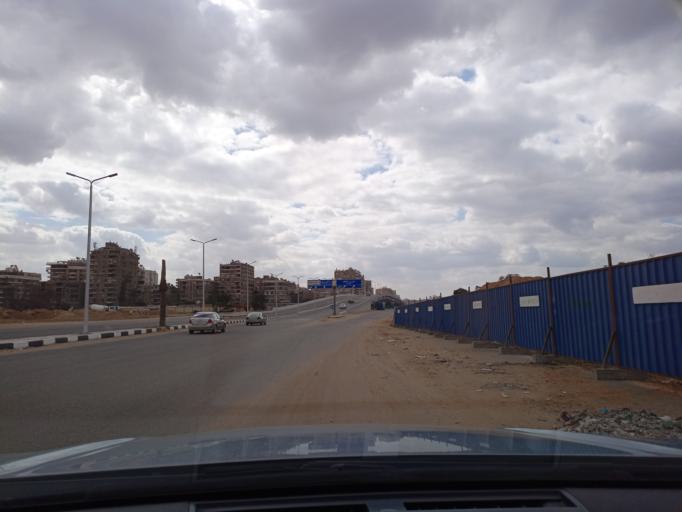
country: EG
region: Muhafazat al Qalyubiyah
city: Al Khankah
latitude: 30.1221
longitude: 31.3540
